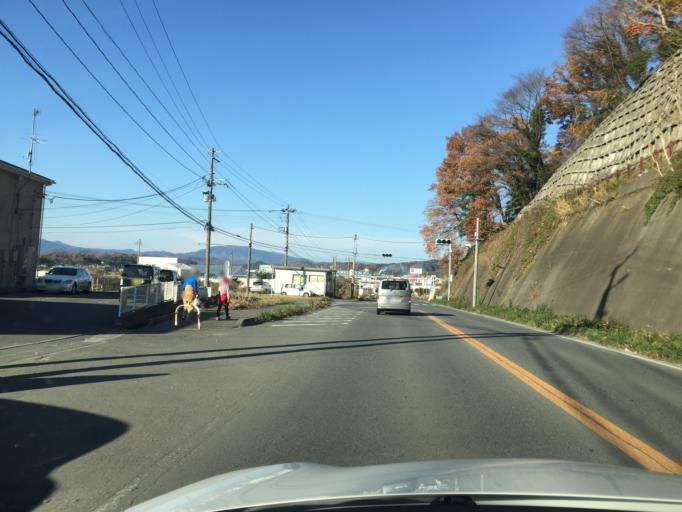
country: JP
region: Fukushima
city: Iwaki
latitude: 36.9702
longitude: 140.8707
